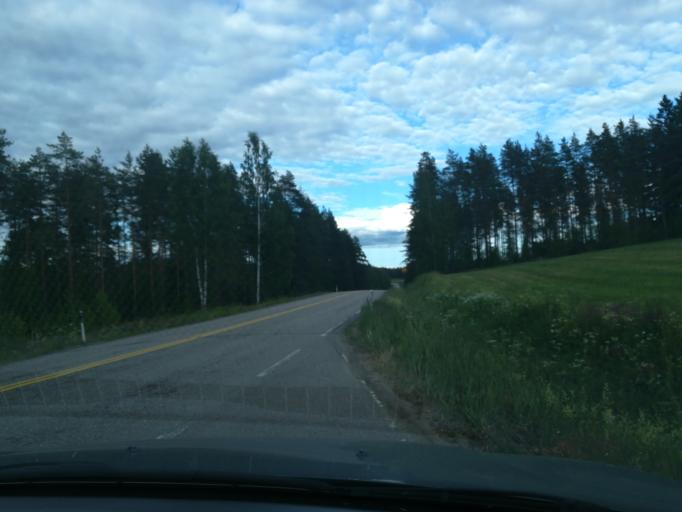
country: FI
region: Southern Savonia
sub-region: Mikkeli
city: Puumala
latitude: 61.5011
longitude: 27.8451
